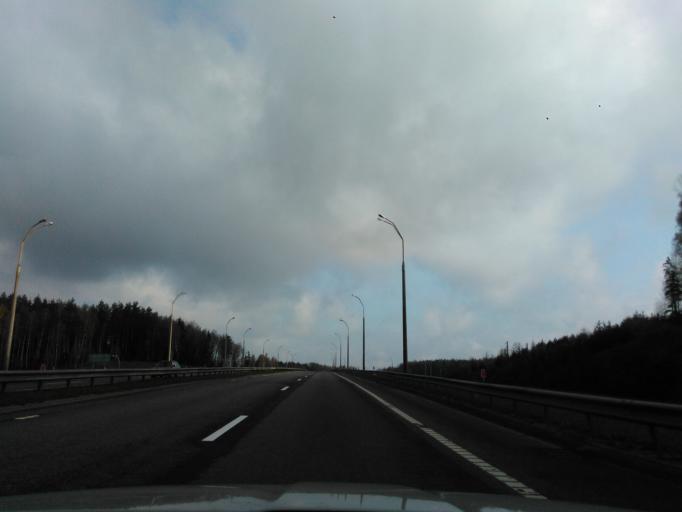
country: BY
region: Minsk
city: Lahoysk
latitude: 54.1799
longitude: 27.8181
